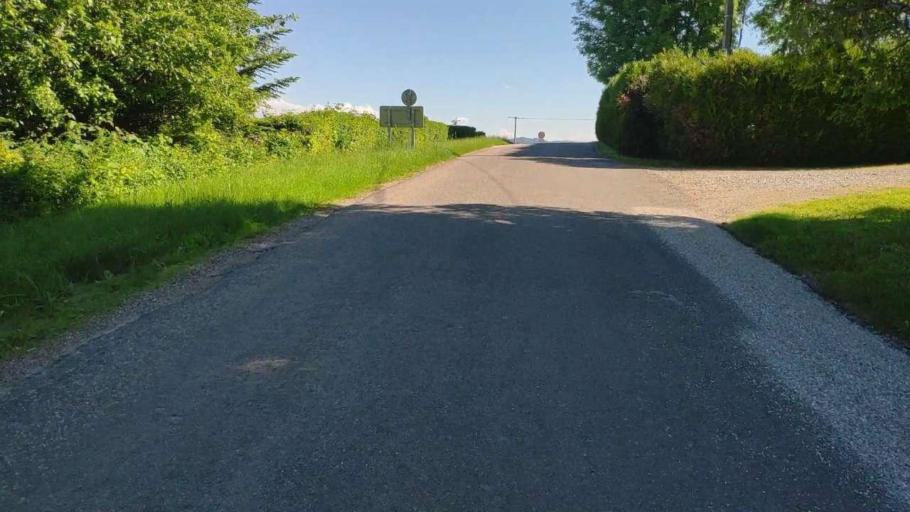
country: FR
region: Franche-Comte
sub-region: Departement du Jura
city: Lons-le-Saunier
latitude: 46.7163
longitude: 5.5626
